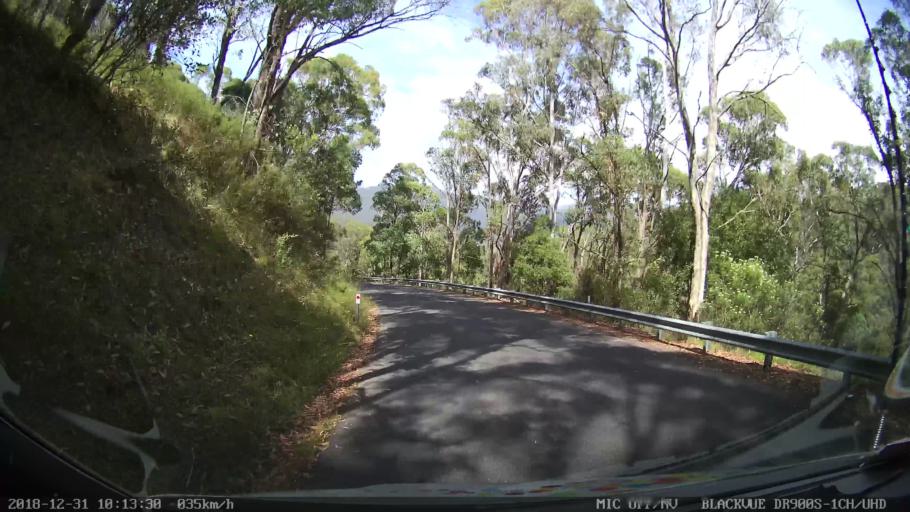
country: AU
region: New South Wales
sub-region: Snowy River
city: Jindabyne
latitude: -36.5380
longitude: 148.1545
